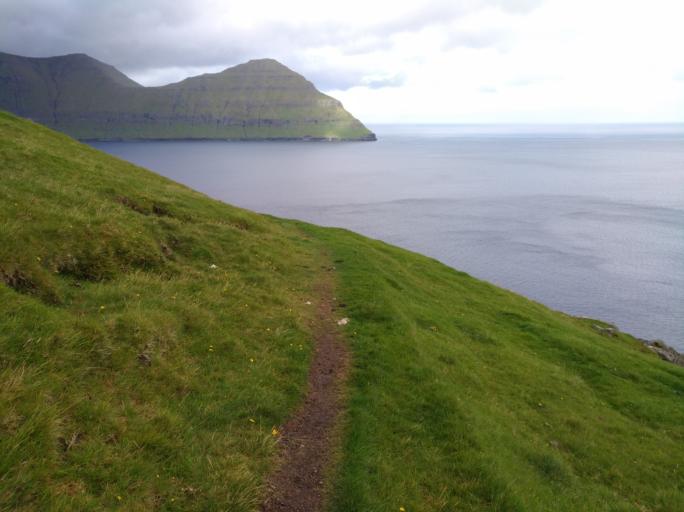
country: FO
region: Eysturoy
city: Fuglafjordur
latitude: 62.2878
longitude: -6.8752
